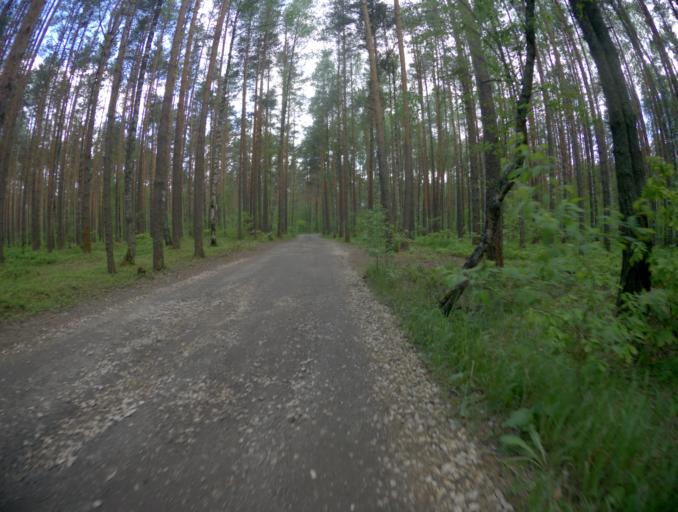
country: RU
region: Vladimir
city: Kommunar
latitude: 56.0994
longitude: 40.4544
